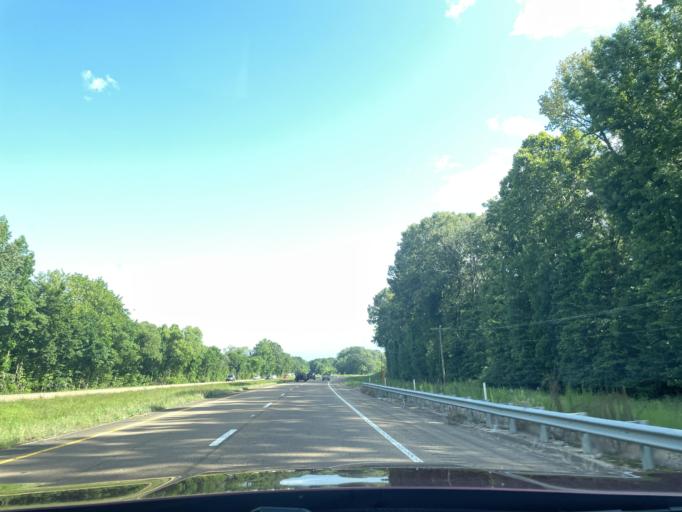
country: US
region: Mississippi
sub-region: Madison County
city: Flora
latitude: 32.4779
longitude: -90.2886
